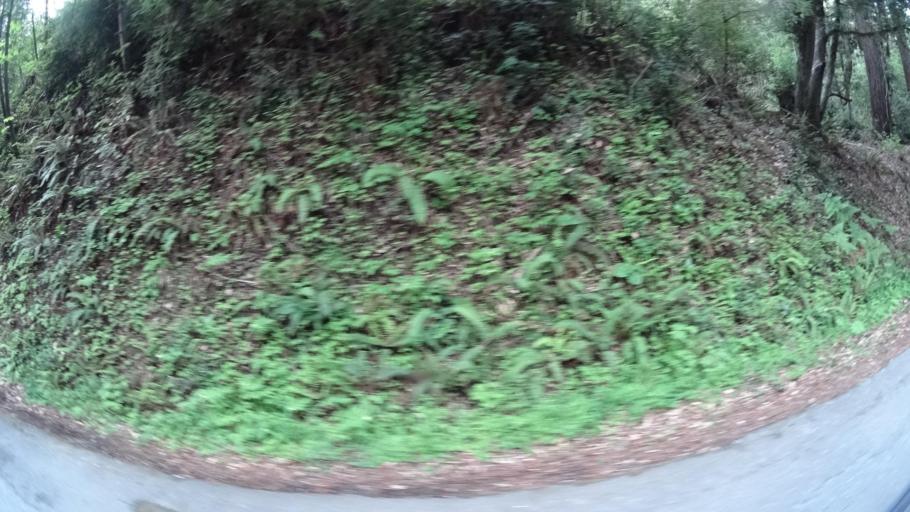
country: US
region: California
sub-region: Humboldt County
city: Redway
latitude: 40.3377
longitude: -123.9116
